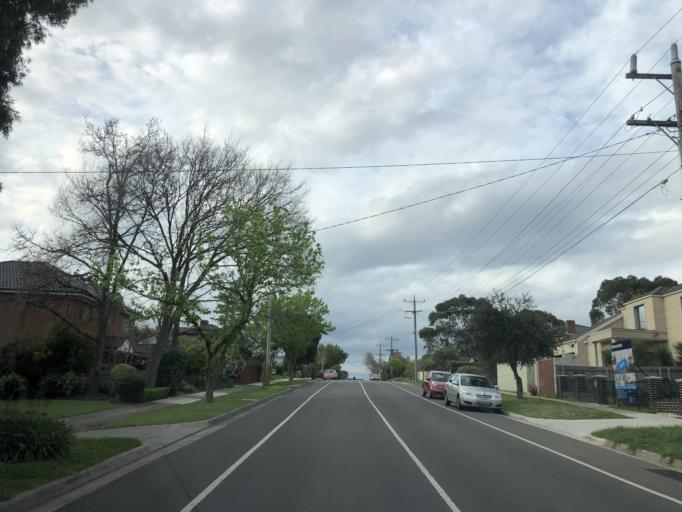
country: AU
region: Victoria
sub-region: Monash
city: Ashwood
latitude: -37.8653
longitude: 145.1191
